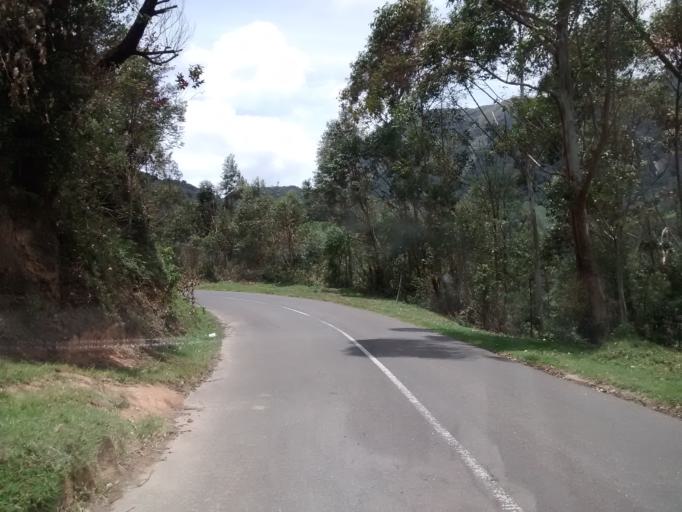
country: IN
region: Kerala
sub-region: Idukki
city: Munnar
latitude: 10.1279
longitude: 77.2041
